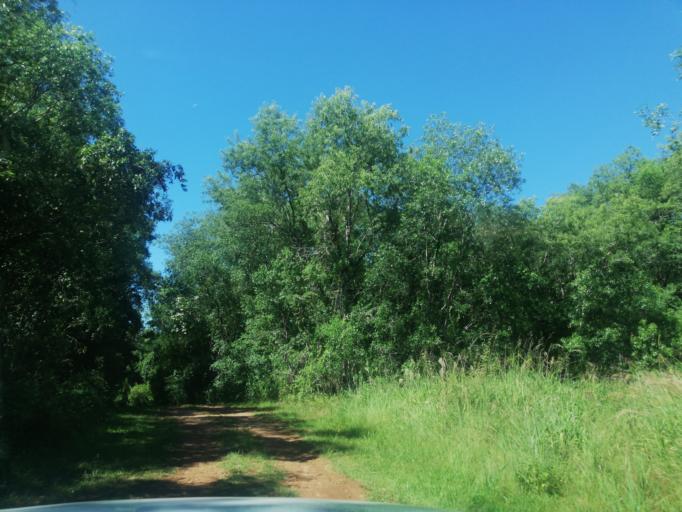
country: AR
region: Misiones
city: Cerro Azul
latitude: -27.7424
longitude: -55.5724
